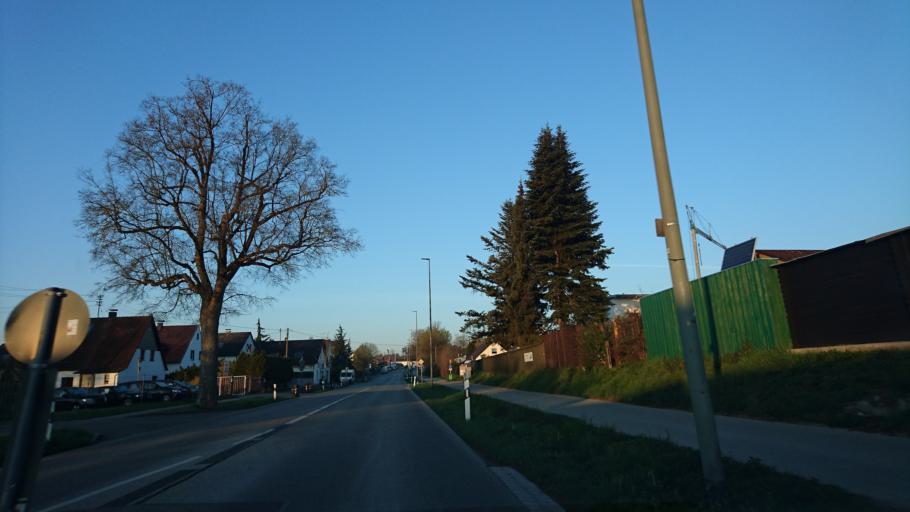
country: DE
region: Bavaria
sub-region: Swabia
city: Stadtbergen
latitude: 48.3745
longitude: 10.8227
